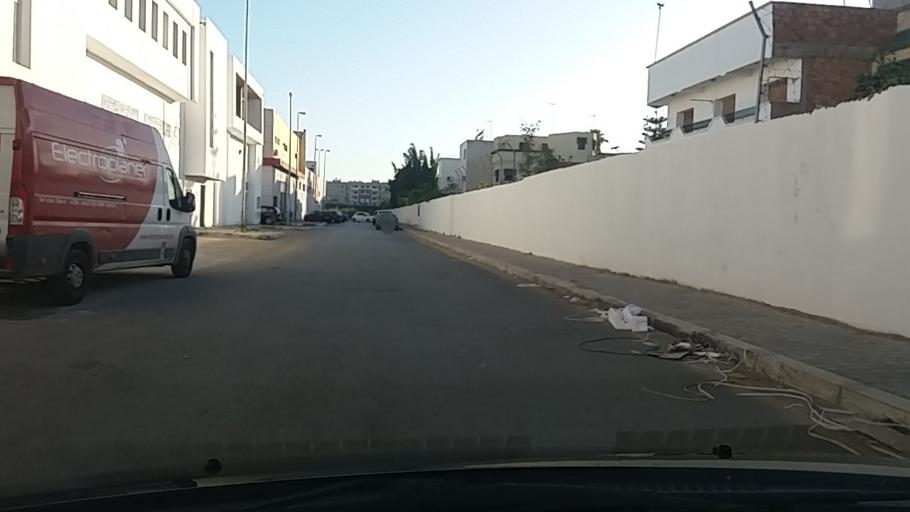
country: MA
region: Gharb-Chrarda-Beni Hssen
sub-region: Kenitra Province
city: Kenitra
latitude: 34.2557
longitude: -6.5984
